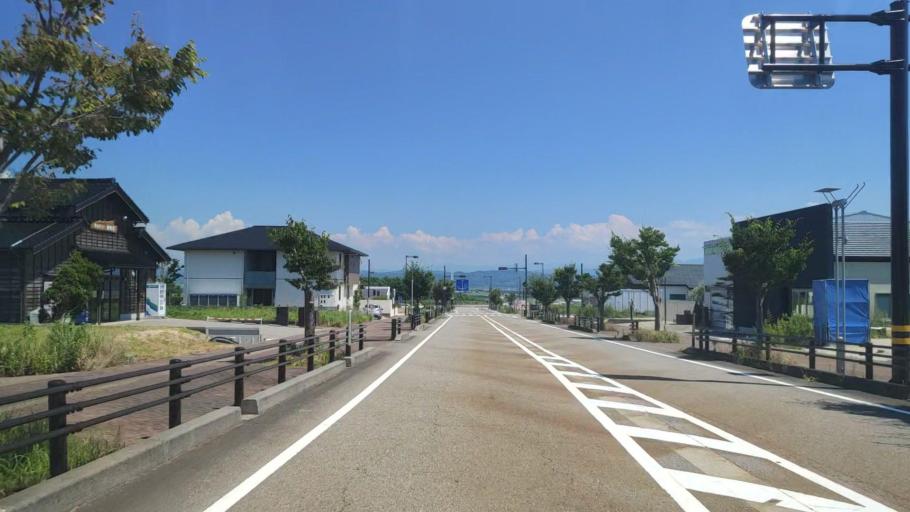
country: JP
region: Ishikawa
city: Tsubata
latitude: 36.6724
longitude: 136.6565
